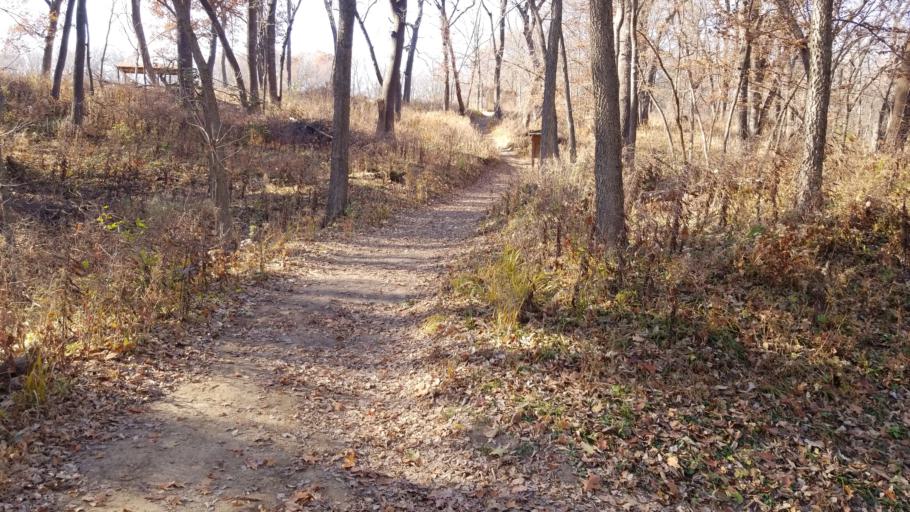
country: US
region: Nebraska
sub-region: Sarpy County
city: Bellevue
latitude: 41.1623
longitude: -95.8945
